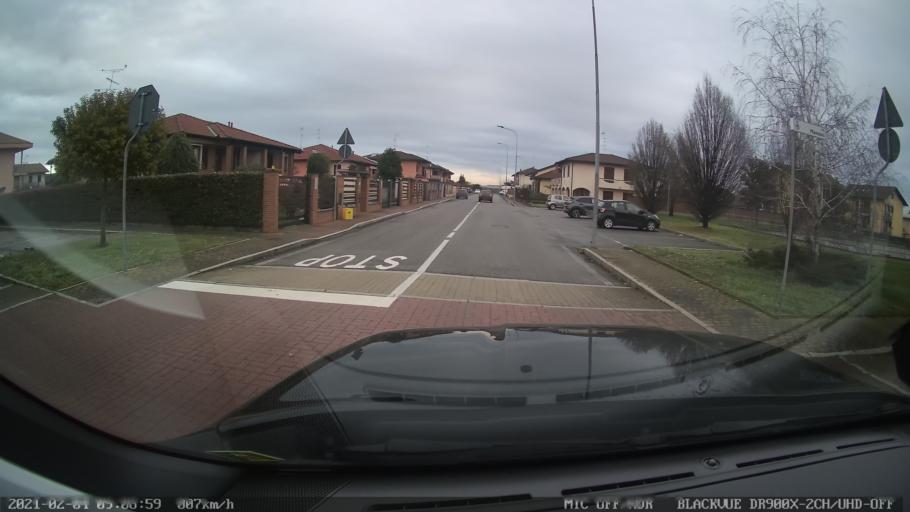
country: IT
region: Piedmont
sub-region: Provincia di Novara
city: San Pietro Mosezzo
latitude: 45.4554
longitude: 8.5461
